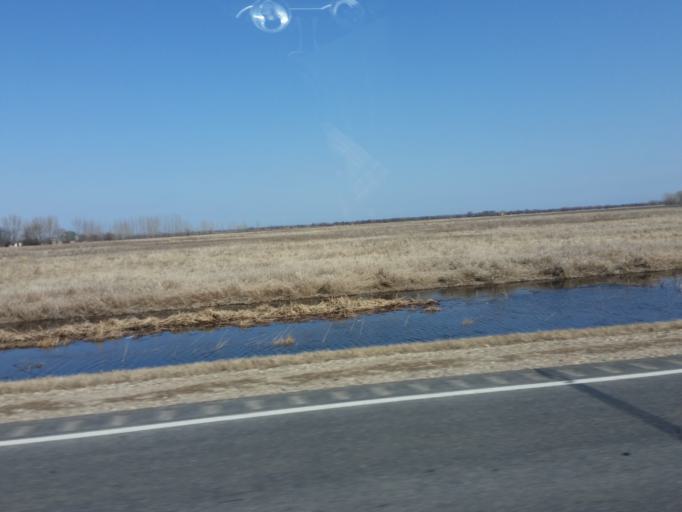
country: US
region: North Dakota
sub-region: Grand Forks County
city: Grand Forks Air Force Base
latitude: 48.1184
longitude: -97.2276
